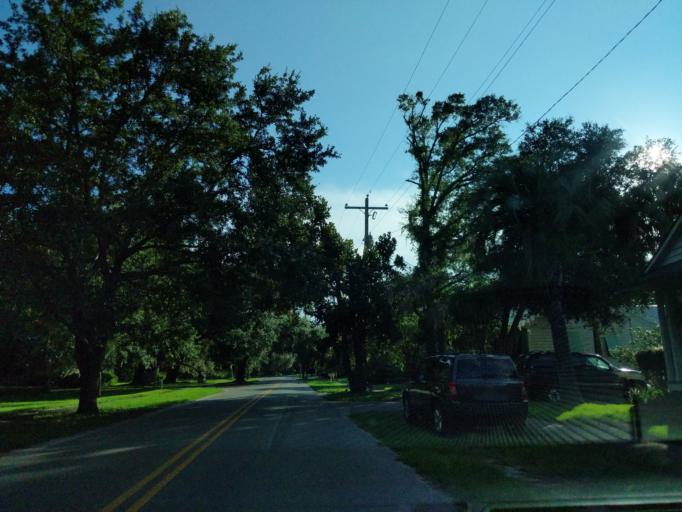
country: US
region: South Carolina
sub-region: Charleston County
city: Awendaw
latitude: 33.0854
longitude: -79.4615
